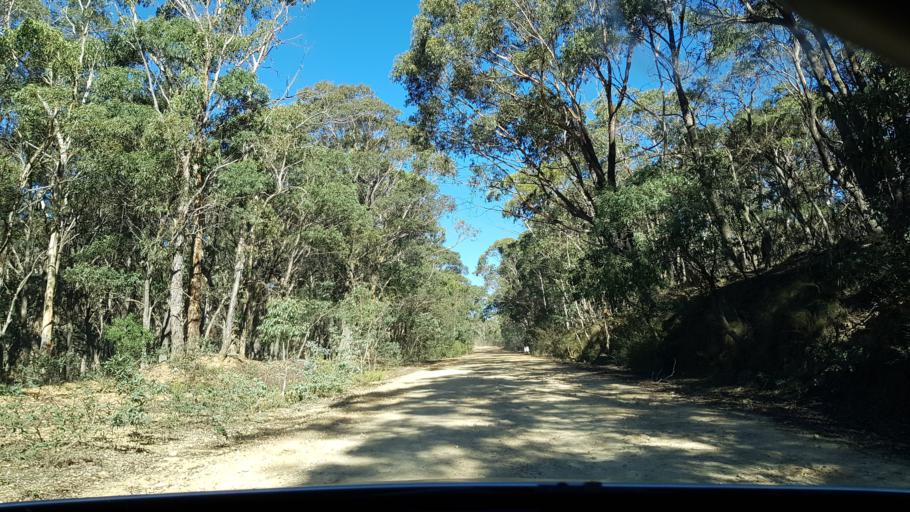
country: AU
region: New South Wales
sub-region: Oberon
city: Oberon
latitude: -33.8467
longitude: 150.0172
